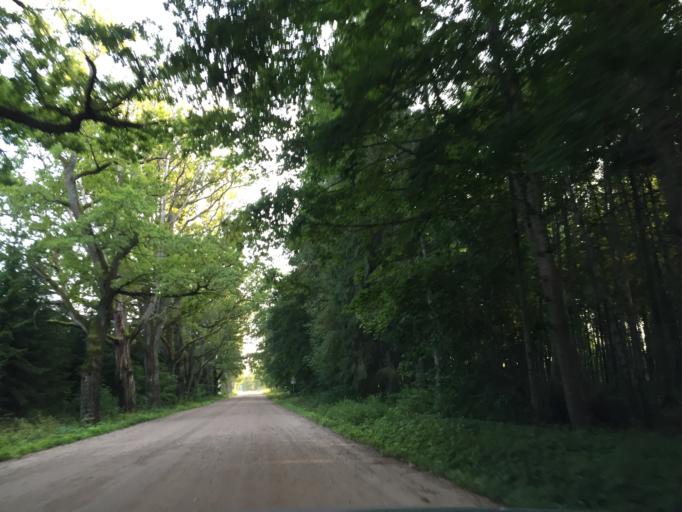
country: LV
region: Limbazu Rajons
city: Limbazi
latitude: 57.5585
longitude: 24.8055
